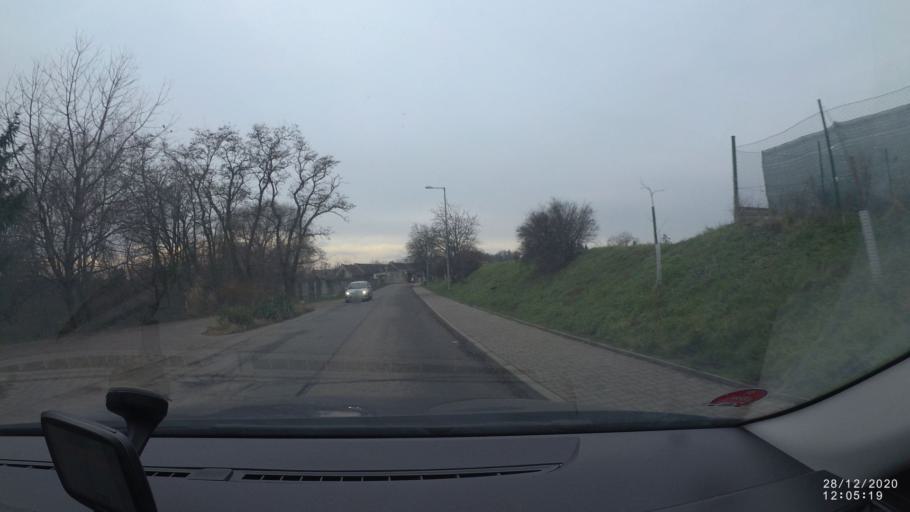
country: CZ
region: Central Bohemia
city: Brandys nad Labem-Stara Boleslav
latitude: 50.1637
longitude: 14.6769
